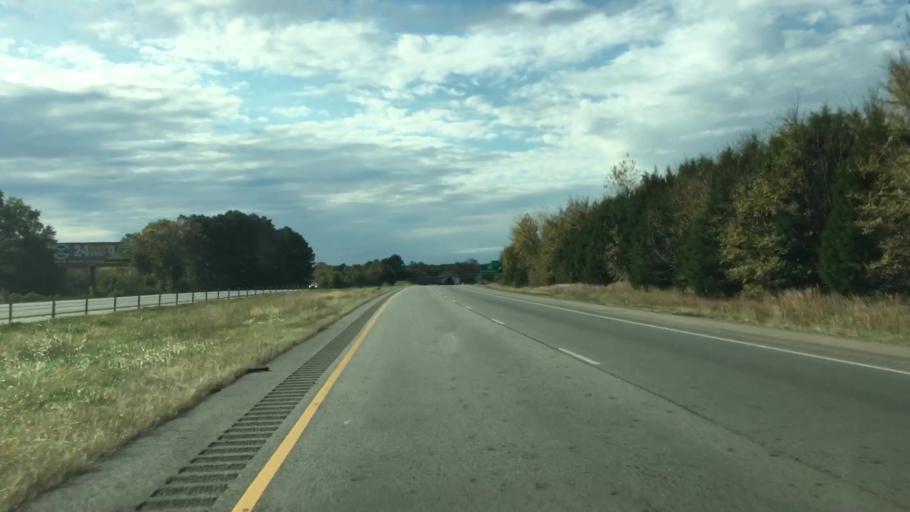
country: US
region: Arkansas
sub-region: Pope County
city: Pottsville
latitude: 35.2485
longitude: -93.0291
